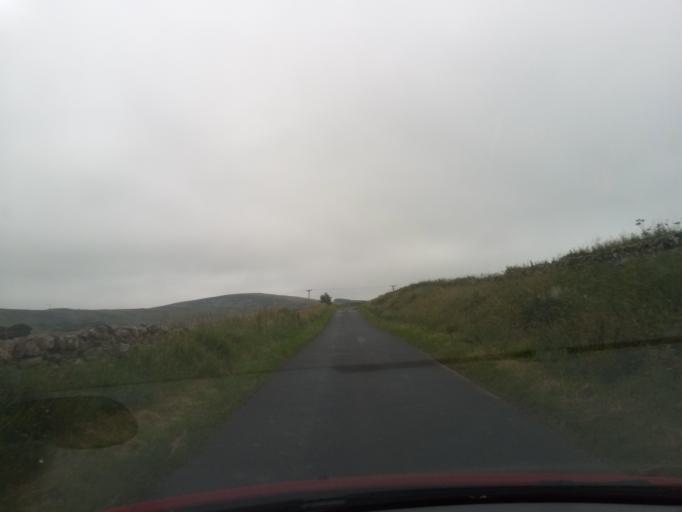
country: GB
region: Scotland
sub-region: The Scottish Borders
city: Galashiels
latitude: 55.6619
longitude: -2.8784
